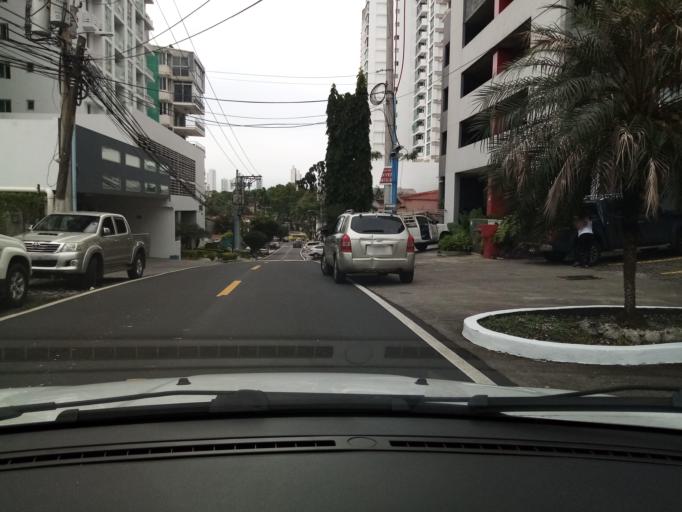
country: PA
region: Panama
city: Panama
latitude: 9.0062
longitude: -79.5064
